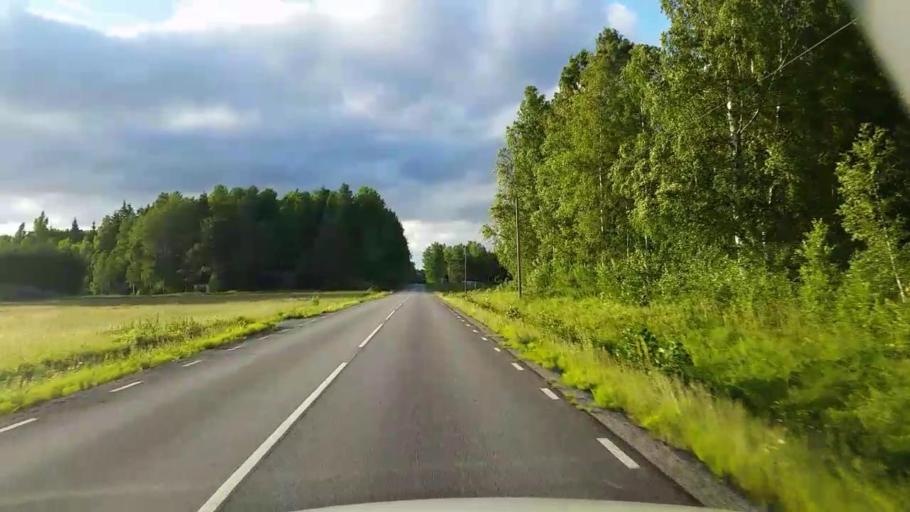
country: SE
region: Vaestmanland
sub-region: Kopings Kommun
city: Kolsva
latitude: 59.7096
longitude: 15.8289
